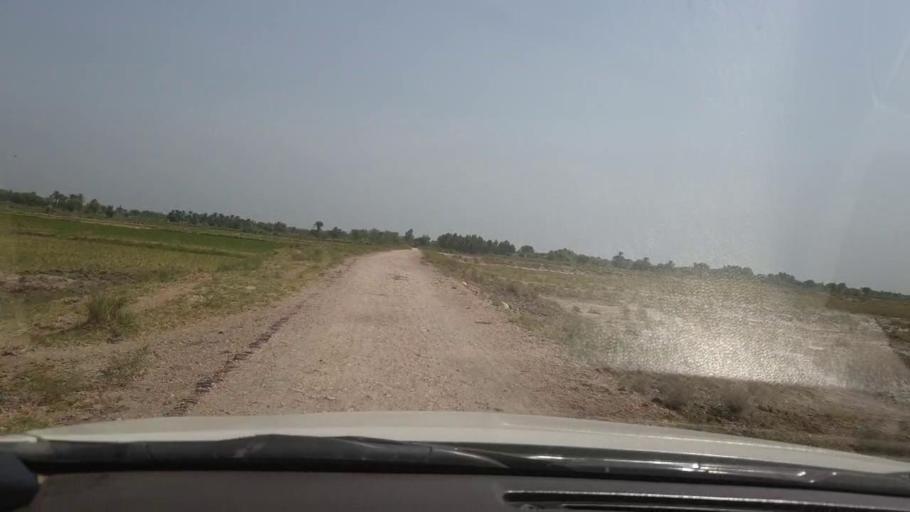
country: PK
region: Sindh
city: Shikarpur
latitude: 27.9230
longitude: 68.6058
